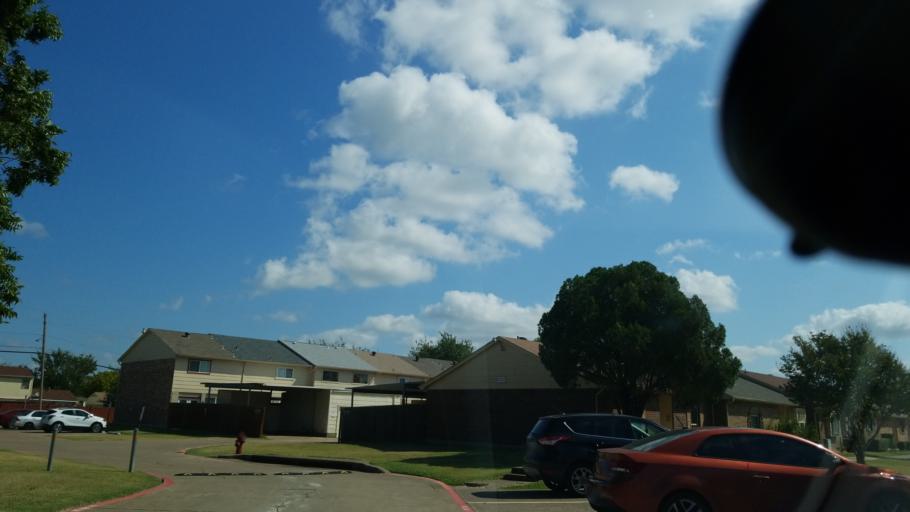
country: US
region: Texas
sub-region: Dallas County
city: Grand Prairie
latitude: 32.6981
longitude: -96.9877
